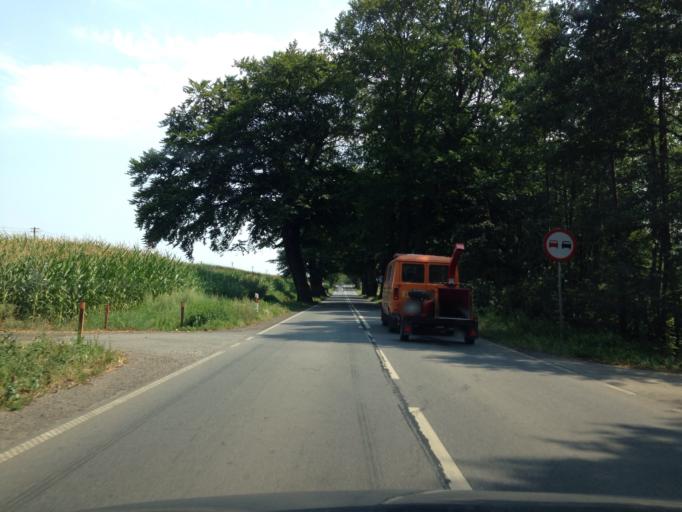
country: PL
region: Kujawsko-Pomorskie
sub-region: Powiat golubsko-dobrzynski
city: Radomin
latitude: 53.0926
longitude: 19.1680
